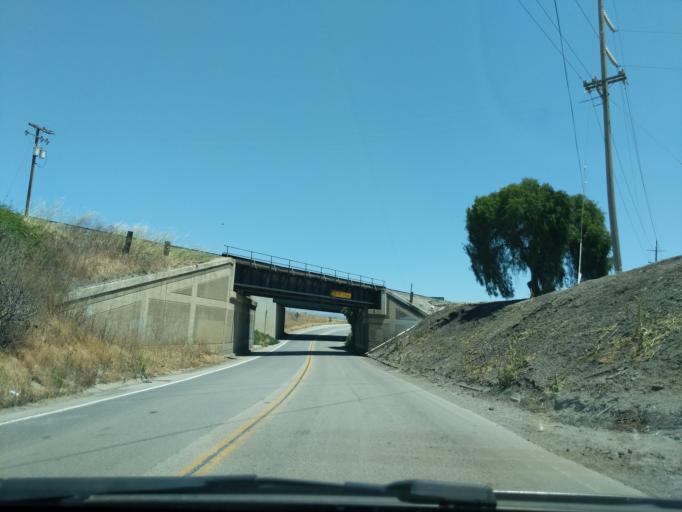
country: US
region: California
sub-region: Monterey County
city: Salinas
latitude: 36.6269
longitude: -121.5876
